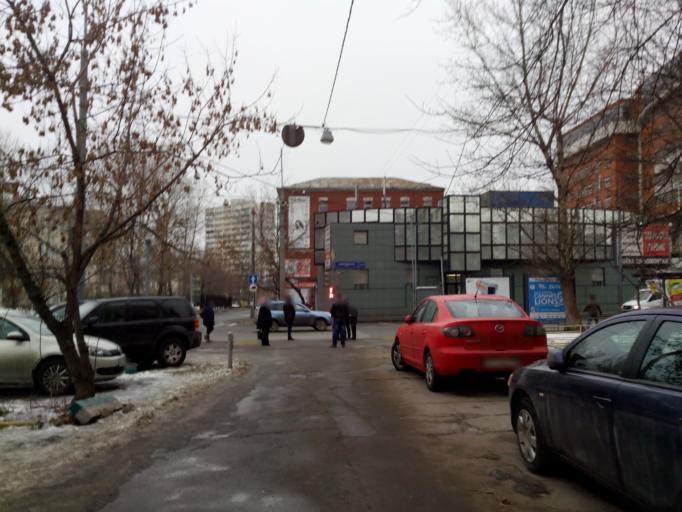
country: RU
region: Moscow
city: Lefortovo
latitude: 55.7775
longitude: 37.6903
